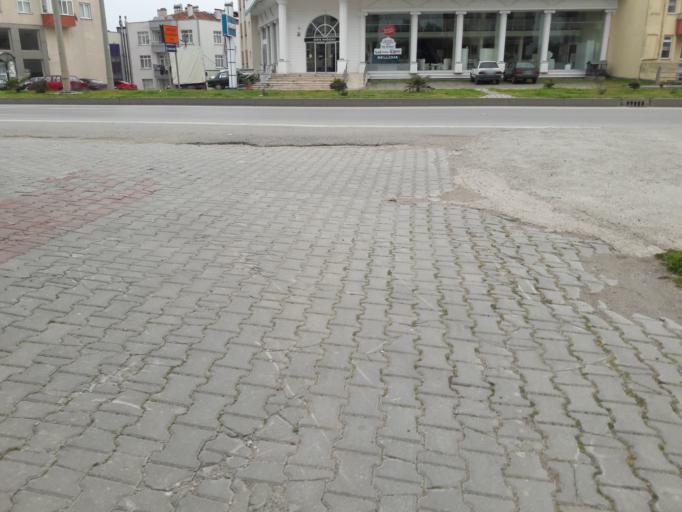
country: TR
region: Sinop
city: Sinop
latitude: 42.0208
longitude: 35.1257
